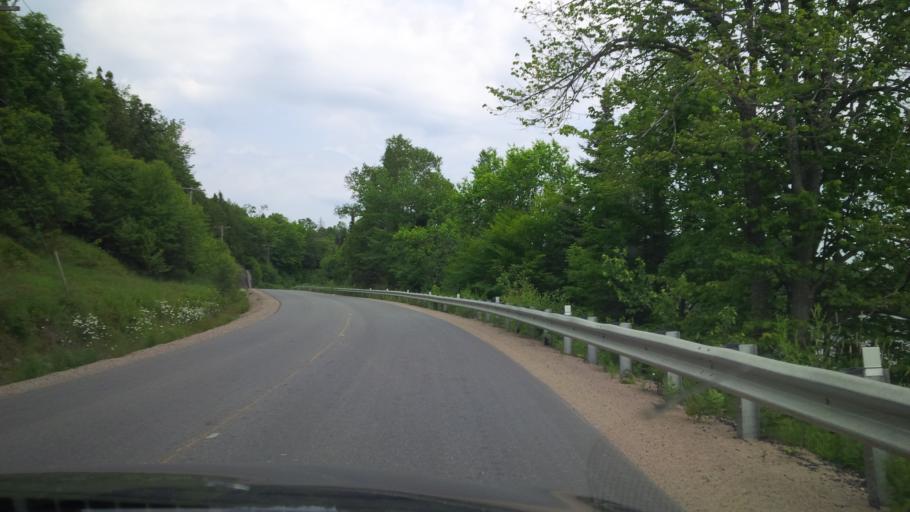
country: CA
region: Ontario
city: Huntsville
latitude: 45.5836
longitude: -79.2168
